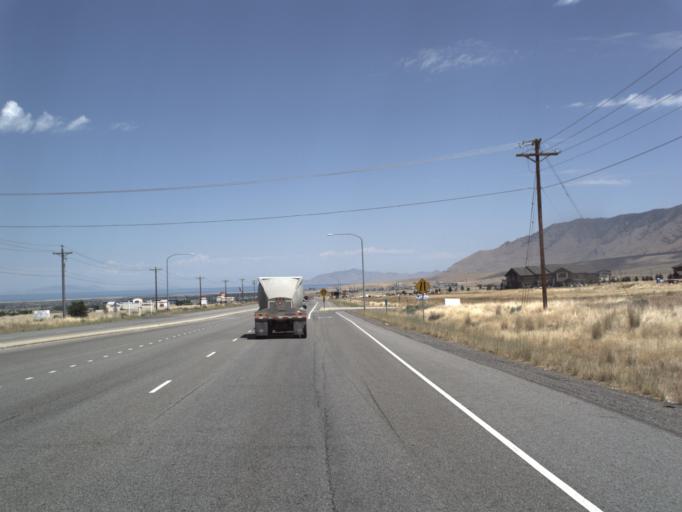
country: US
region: Utah
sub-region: Tooele County
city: Tooele
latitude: 40.5648
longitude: -112.2959
